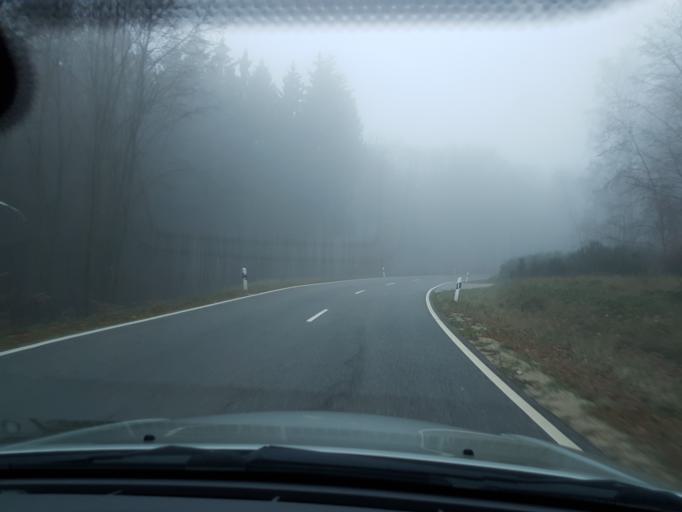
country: DE
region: Hesse
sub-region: Regierungsbezirk Darmstadt
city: Schlangenbad
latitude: 50.0781
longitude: 8.0475
